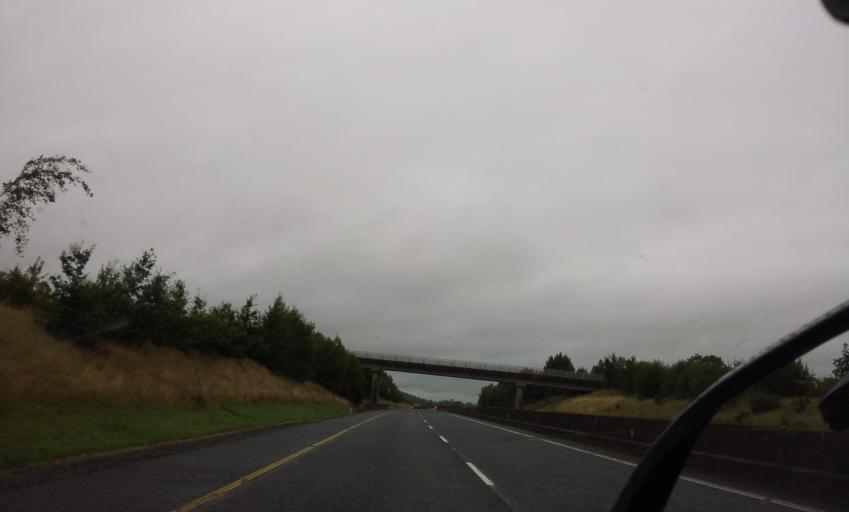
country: IE
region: Munster
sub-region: County Cork
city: Rathcormac
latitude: 52.0865
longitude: -8.2942
